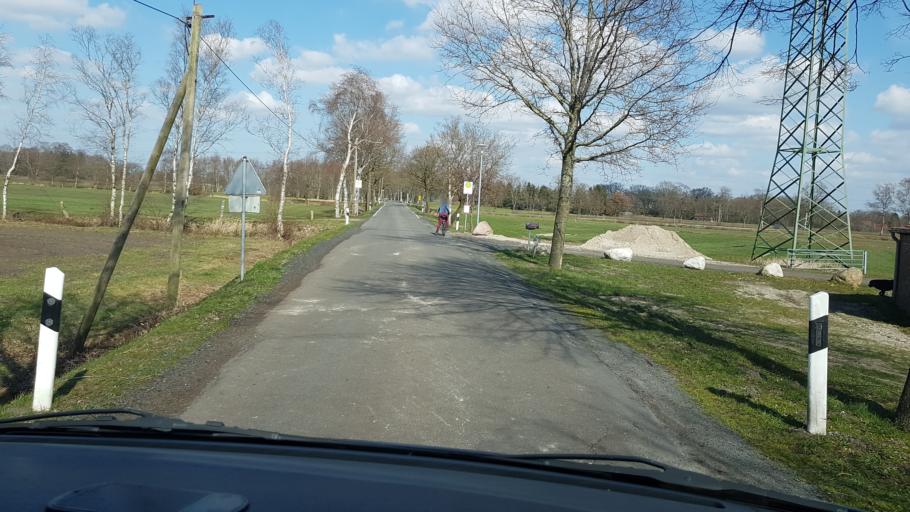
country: DE
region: Lower Saxony
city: Rastede
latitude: 53.2951
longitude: 8.1948
